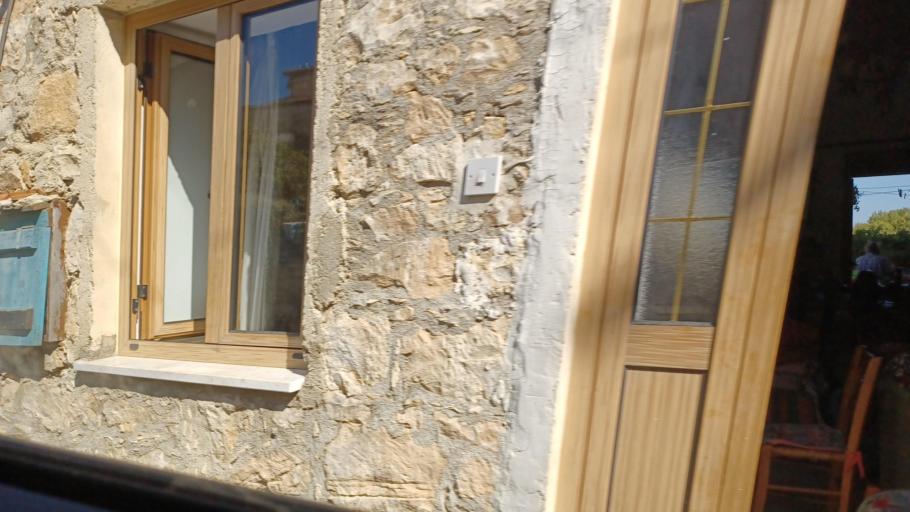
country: CY
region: Pafos
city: Mesogi
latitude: 34.9300
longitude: 32.5443
